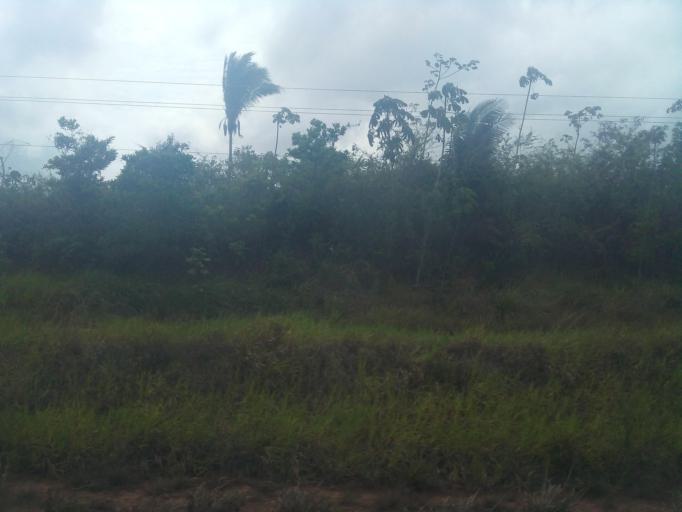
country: BR
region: Maranhao
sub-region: Itapecuru Mirim
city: Itapecuru Mirim
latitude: -3.1707
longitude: -44.3626
